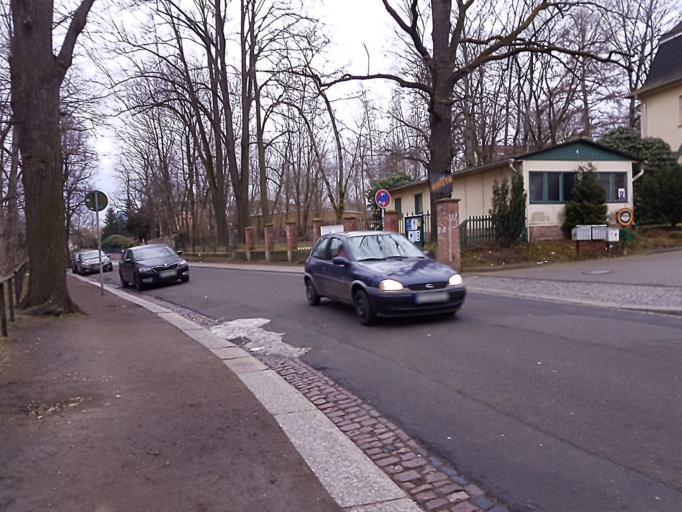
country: DE
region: Saxony
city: Chemnitz
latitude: 50.8352
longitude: 12.9124
